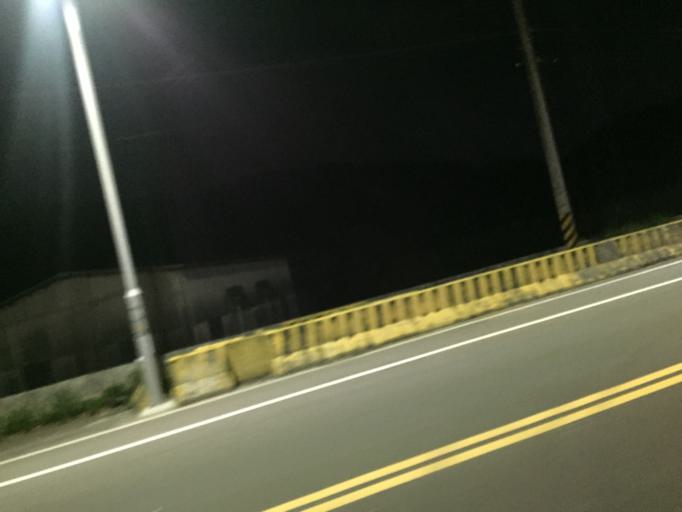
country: TW
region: Taiwan
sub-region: Hsinchu
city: Hsinchu
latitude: 24.7567
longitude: 120.9743
